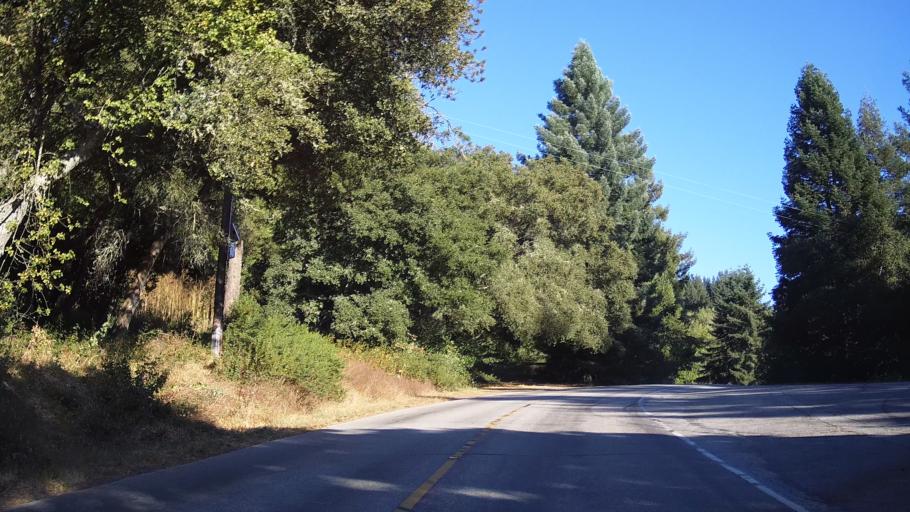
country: US
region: California
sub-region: Alameda County
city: Berkeley
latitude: 37.8832
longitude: -122.2270
